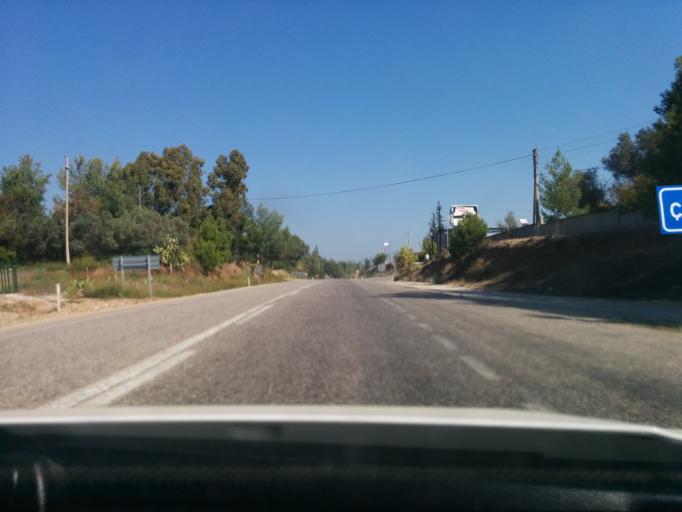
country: TR
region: Mugla
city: Kemer
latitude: 36.5502
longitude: 29.3448
